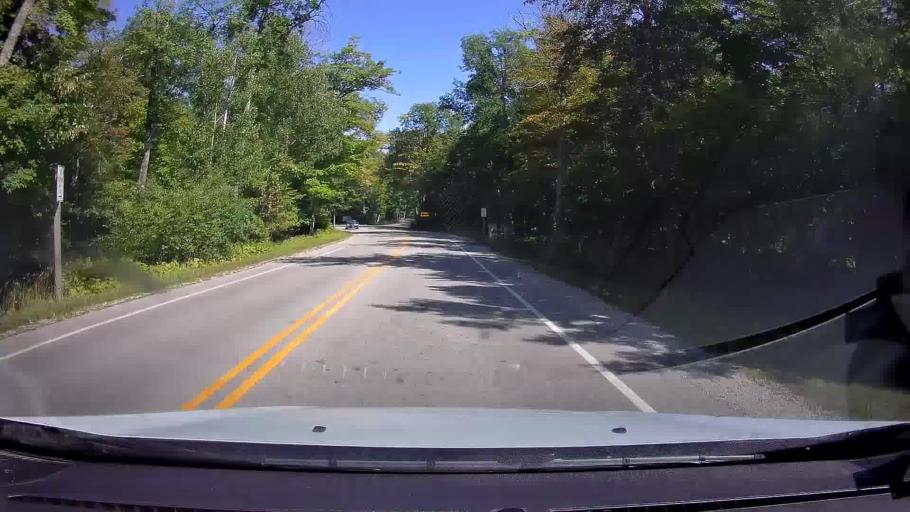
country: US
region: Michigan
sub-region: Delta County
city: Escanaba
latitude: 45.2893
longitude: -86.9816
